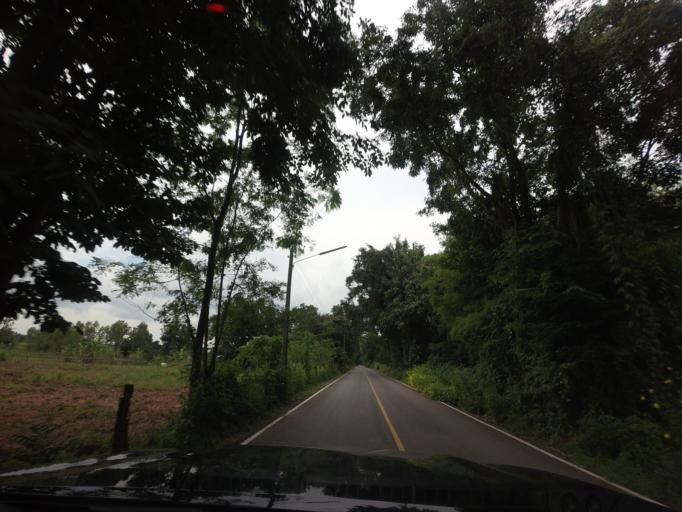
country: TH
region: Changwat Nong Bua Lamphu
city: Nong Bua Lamphu
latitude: 17.2516
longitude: 102.3854
